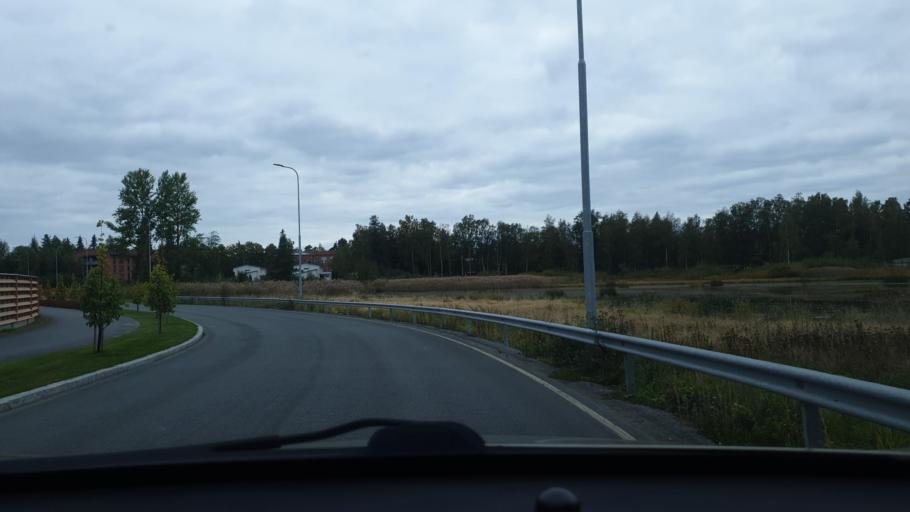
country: FI
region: Ostrobothnia
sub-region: Vaasa
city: Vaasa
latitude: 63.1197
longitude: 21.6238
